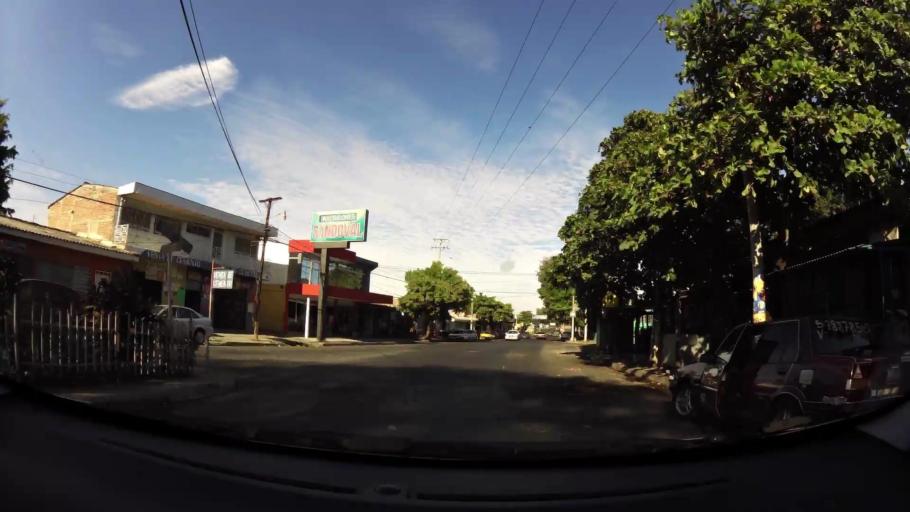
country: SV
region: Santa Ana
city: Santa Ana
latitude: 14.0007
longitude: -89.5511
